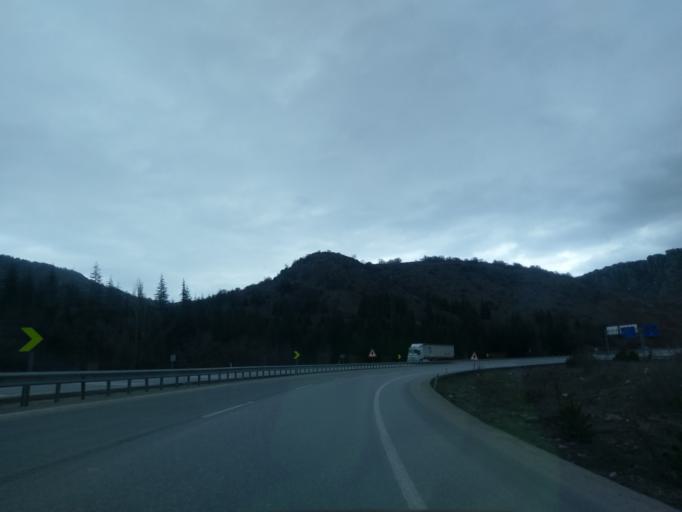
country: TR
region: Kuetahya
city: Sabuncu
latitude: 39.5766
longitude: 30.0854
